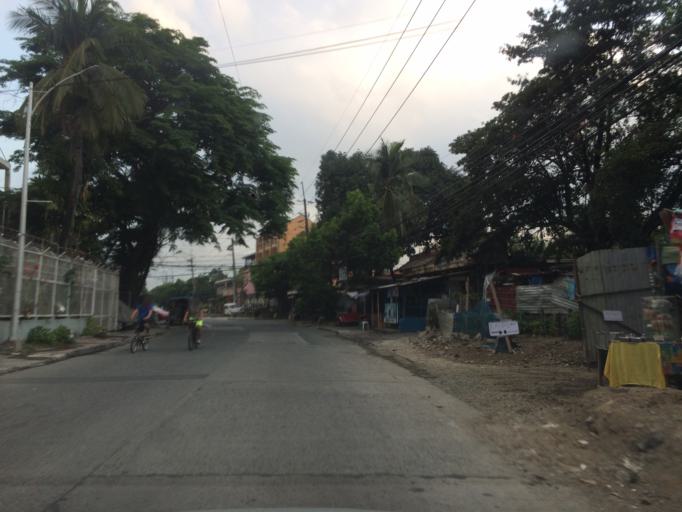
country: PH
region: Calabarzon
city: Bagong Pagasa
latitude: 14.6755
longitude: 121.0262
